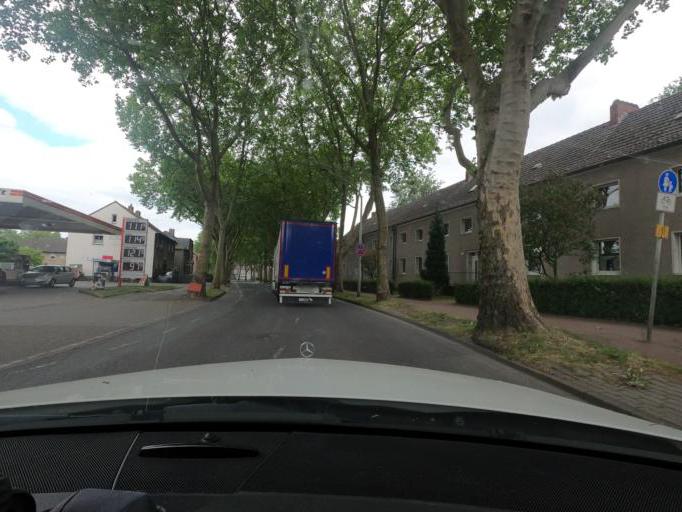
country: DE
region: North Rhine-Westphalia
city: Meiderich
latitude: 51.4801
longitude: 6.7440
